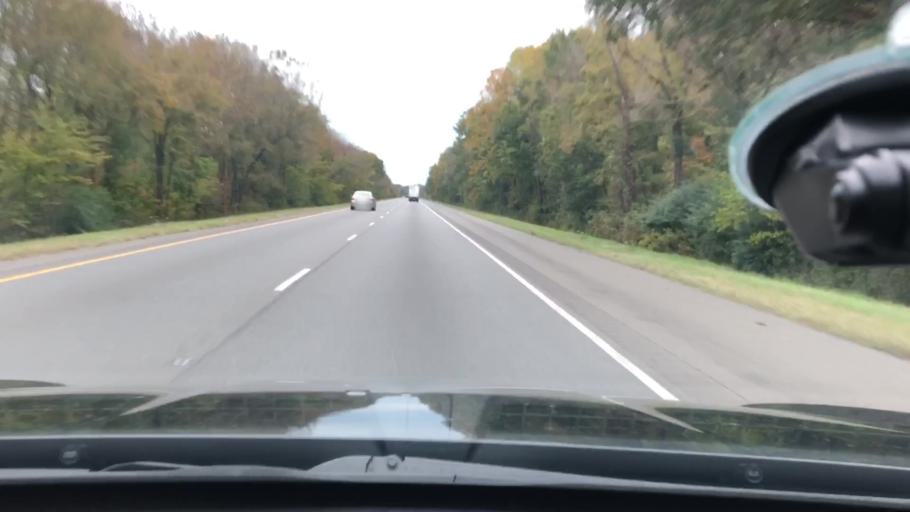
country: US
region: Arkansas
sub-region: Hempstead County
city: Hope
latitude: 33.6543
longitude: -93.6598
